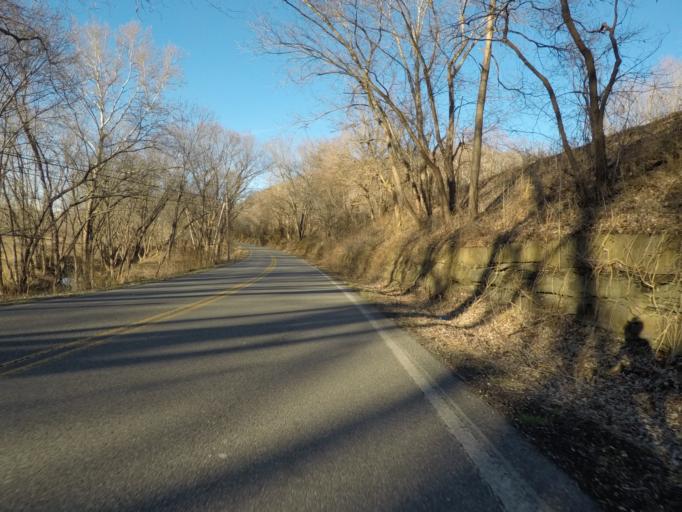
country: US
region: West Virginia
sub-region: Wayne County
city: Kenova
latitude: 38.3744
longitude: -82.5903
